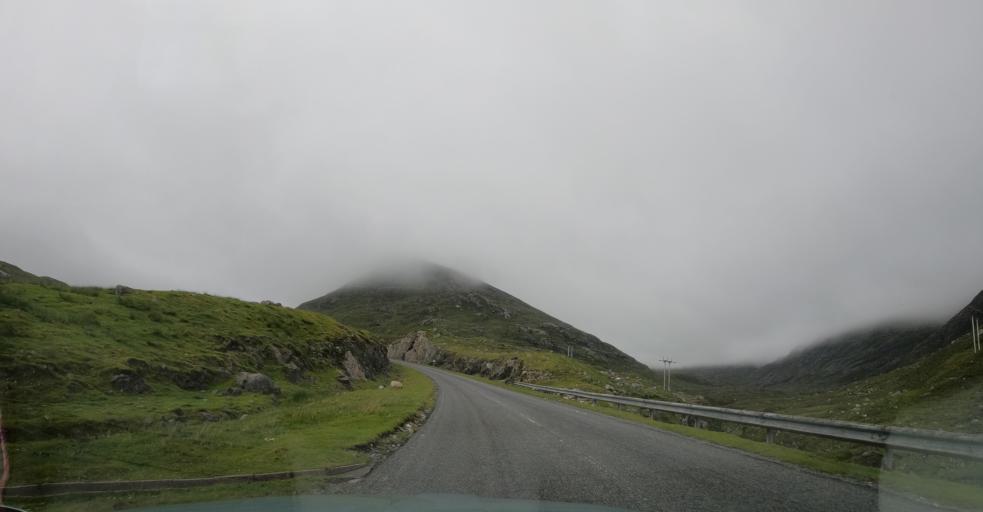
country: GB
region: Scotland
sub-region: Eilean Siar
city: Harris
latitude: 57.9279
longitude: -6.8357
